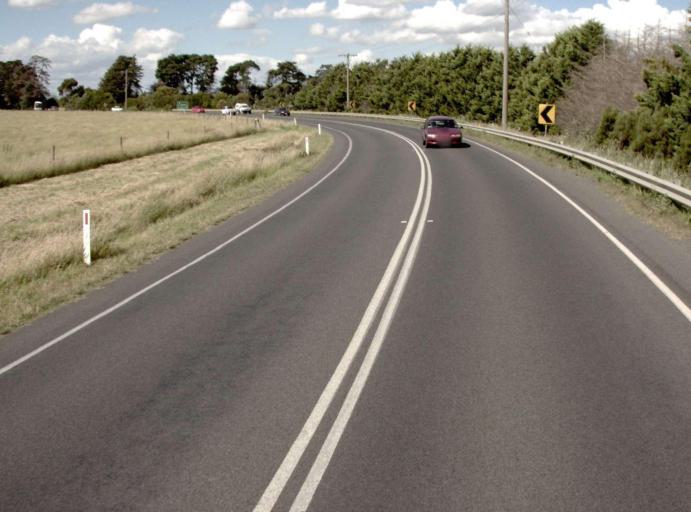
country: AU
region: Victoria
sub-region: Latrobe
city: Morwell
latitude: -38.2937
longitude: 146.4279
